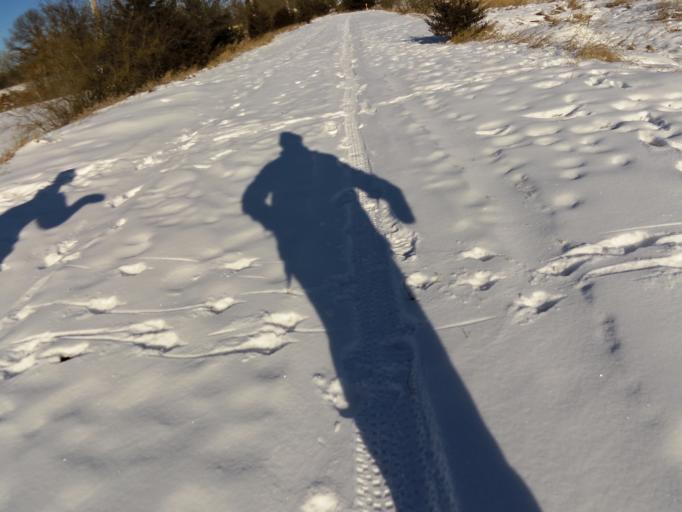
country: US
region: Minnesota
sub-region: Washington County
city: Lake Elmo
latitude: 44.9952
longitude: -92.8983
